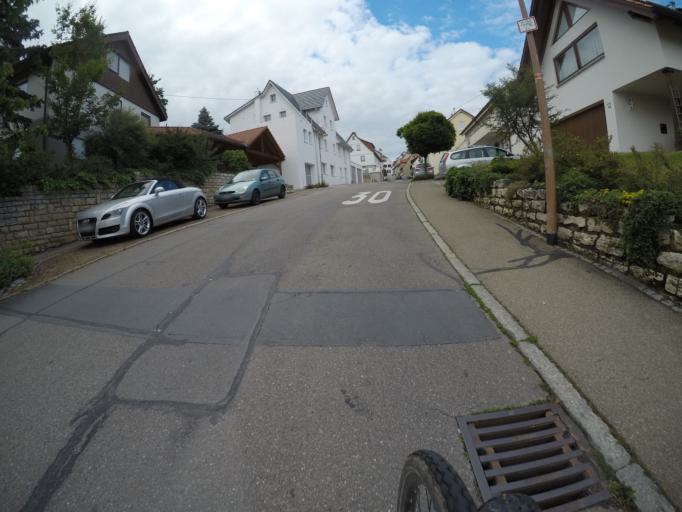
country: DE
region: Baden-Wuerttemberg
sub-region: Regierungsbezirk Stuttgart
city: Grossbettlingen
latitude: 48.5680
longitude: 9.3060
